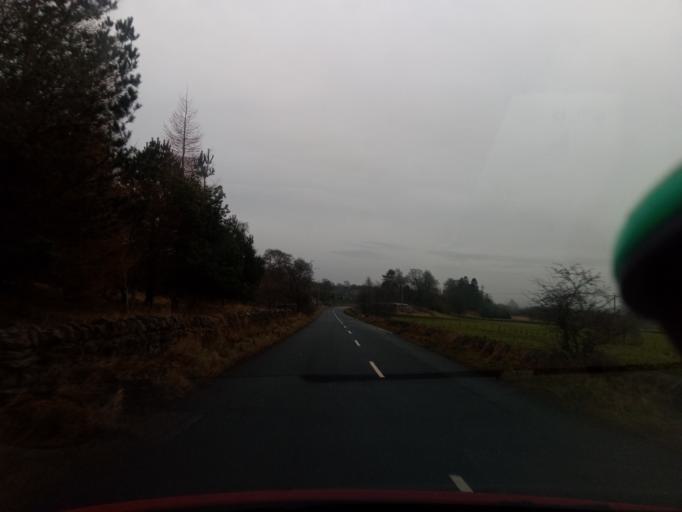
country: GB
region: England
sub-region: Northumberland
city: Rochester
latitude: 55.1603
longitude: -2.3066
